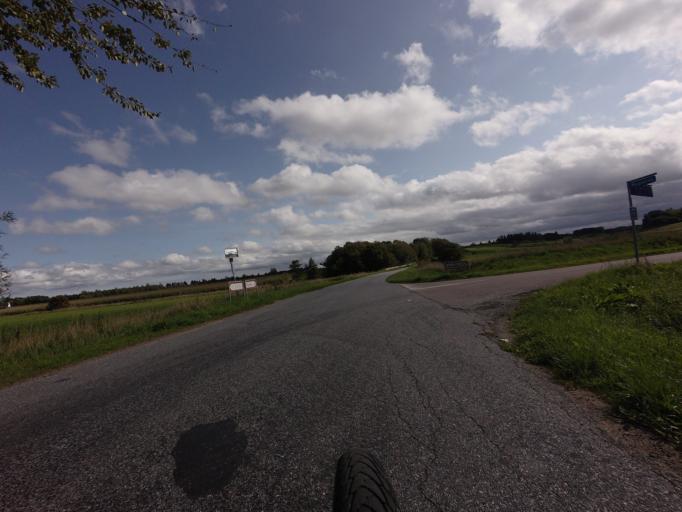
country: DK
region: North Denmark
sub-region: Hjorring Kommune
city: Hirtshals
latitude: 57.5518
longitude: 10.0612
